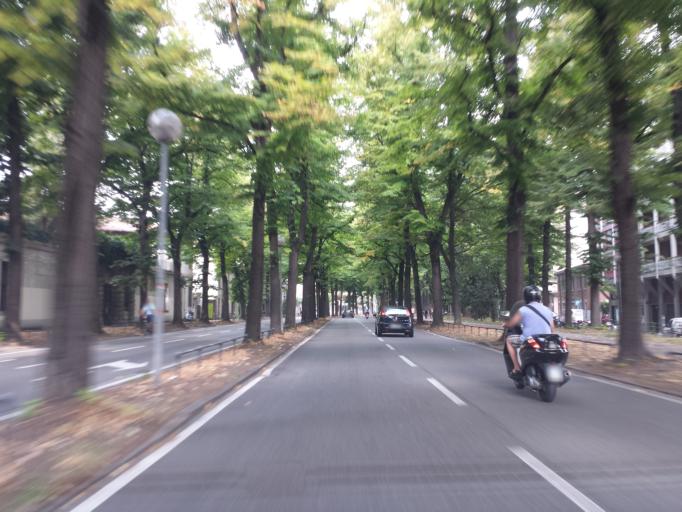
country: IT
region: Veneto
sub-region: Provincia di Padova
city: Padova
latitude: 45.4078
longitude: 11.8852
